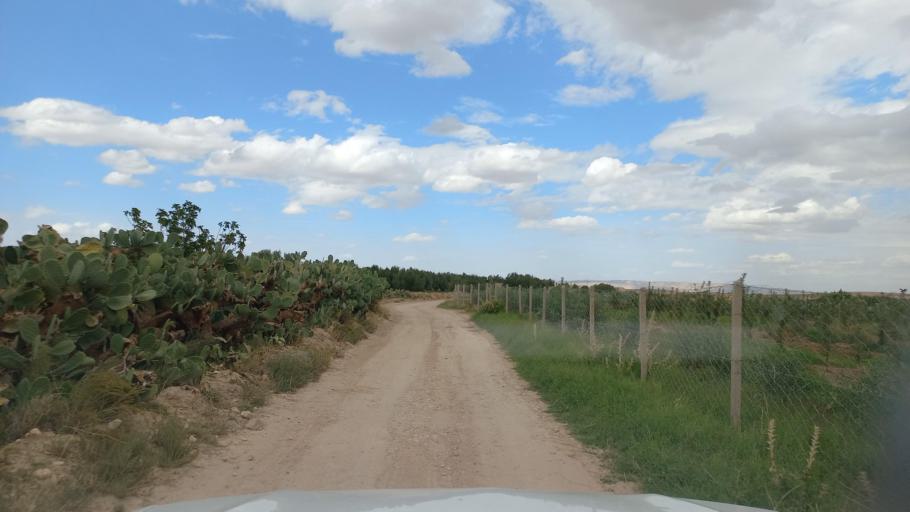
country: TN
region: Al Qasrayn
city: Sbiba
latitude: 35.4373
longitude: 9.0988
